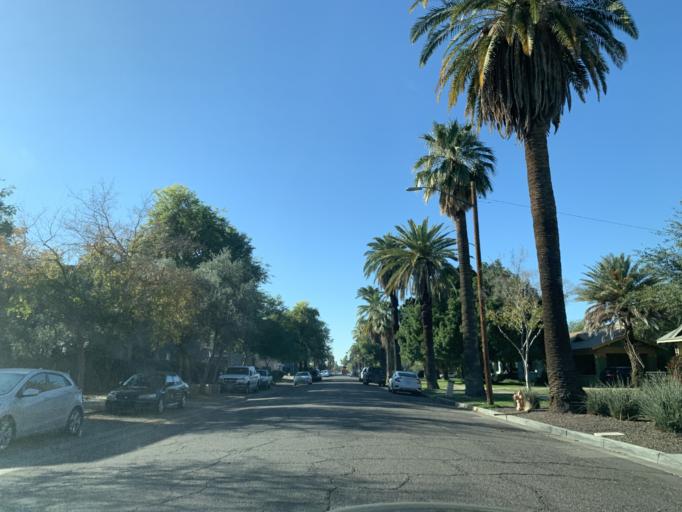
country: US
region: Arizona
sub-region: Maricopa County
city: Phoenix
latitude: 33.4600
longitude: -112.0662
